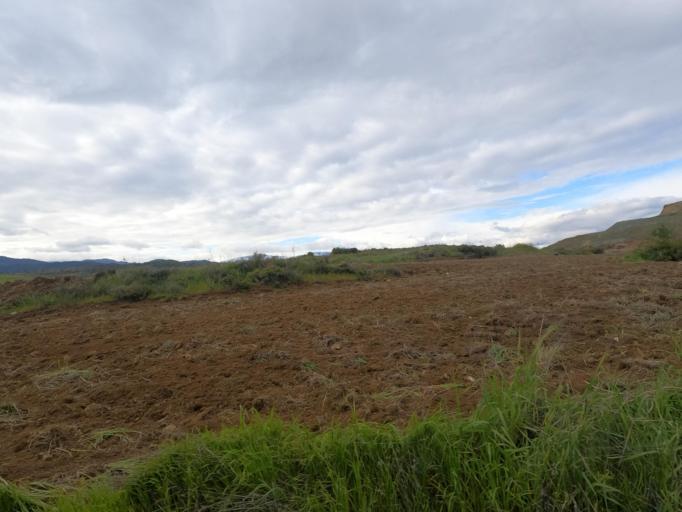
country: CY
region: Lefkosia
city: Lefka
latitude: 35.0904
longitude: 32.9069
